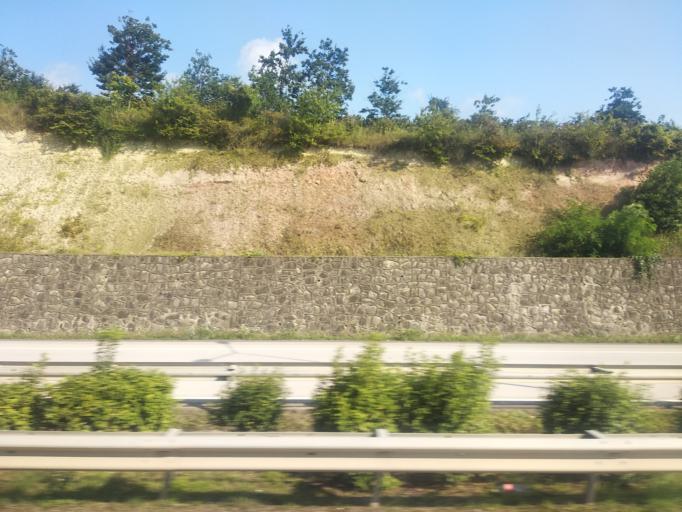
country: TR
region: Ordu
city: Ordu
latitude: 41.0033
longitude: 37.8254
